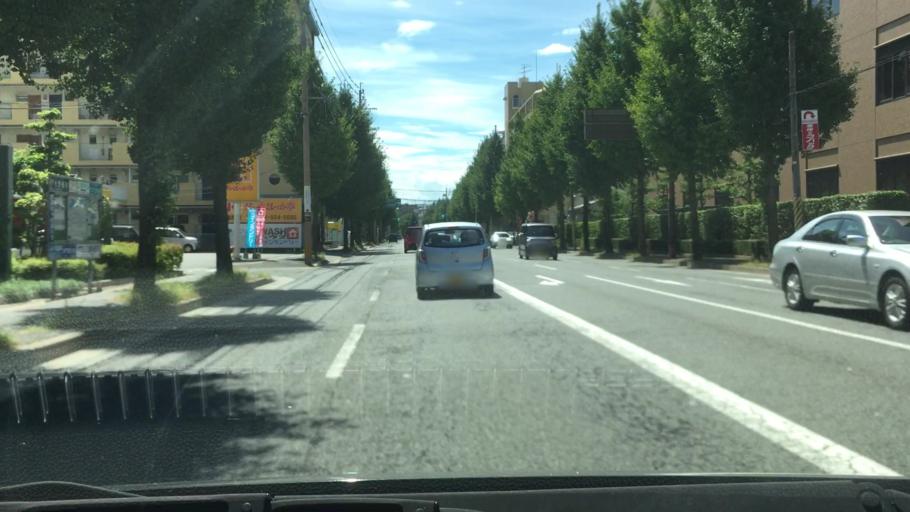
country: JP
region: Fukuoka
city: Fukuoka-shi
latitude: 33.5678
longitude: 130.4265
